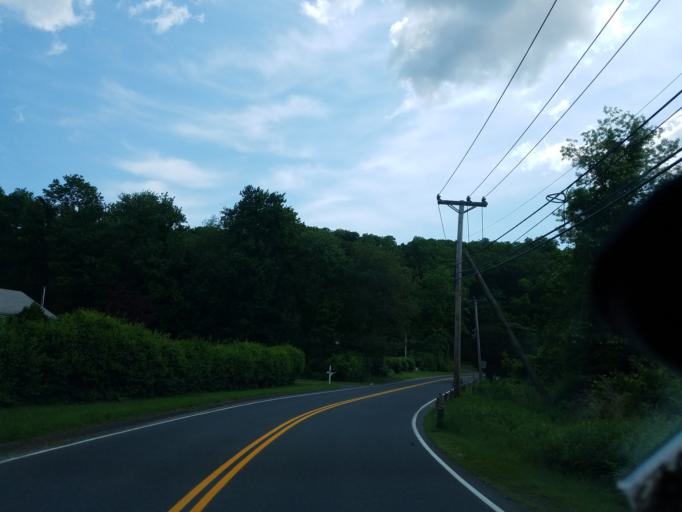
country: US
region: New York
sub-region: Putnam County
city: Putnam Lake
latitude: 41.4678
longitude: -73.5258
